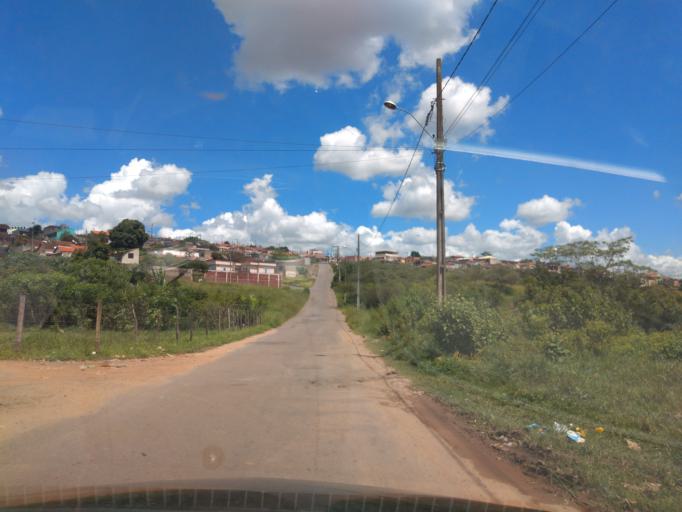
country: BR
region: Minas Gerais
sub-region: Tres Coracoes
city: Tres Coracoes
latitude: -21.6807
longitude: -45.2474
